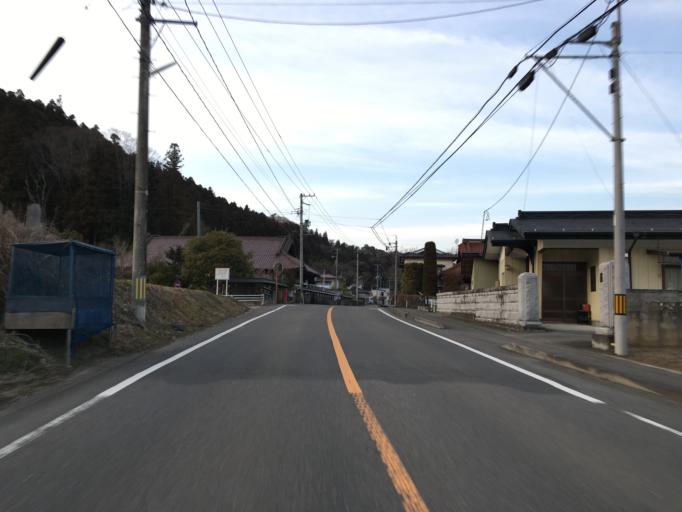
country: JP
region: Ibaraki
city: Daigo
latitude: 36.9011
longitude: 140.4070
